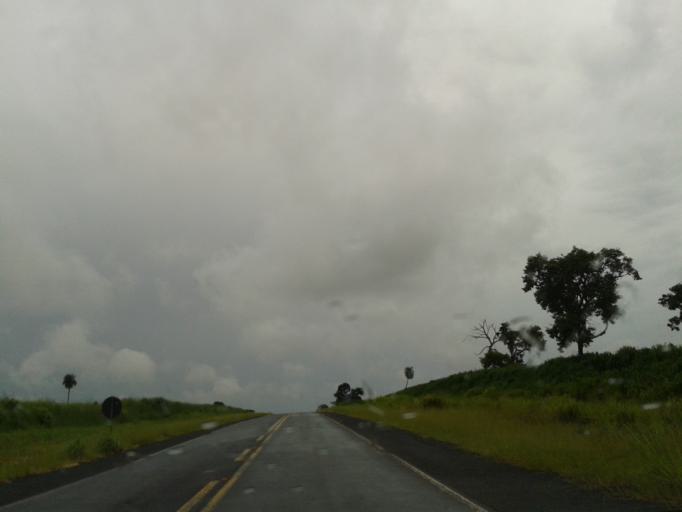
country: BR
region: Minas Gerais
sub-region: Santa Vitoria
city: Santa Vitoria
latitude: -19.1561
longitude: -50.1273
